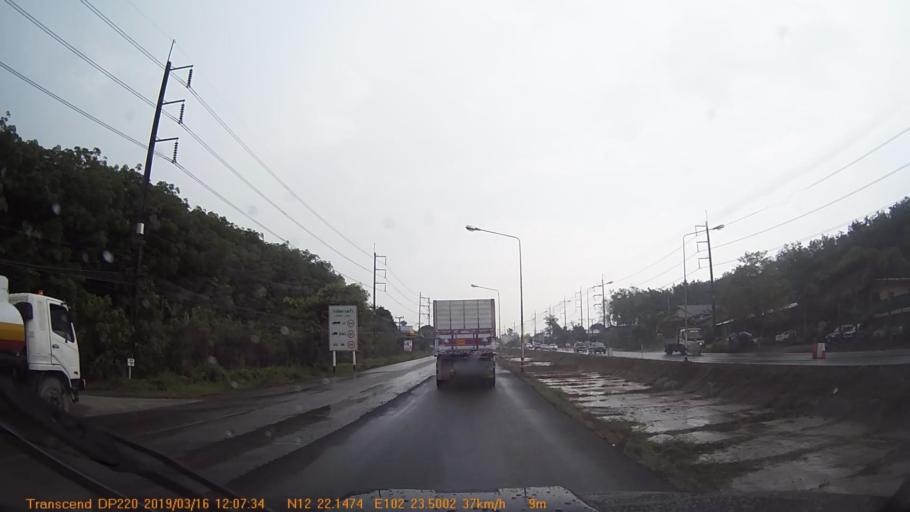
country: TH
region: Trat
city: Khao Saming
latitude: 12.3665
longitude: 102.4012
